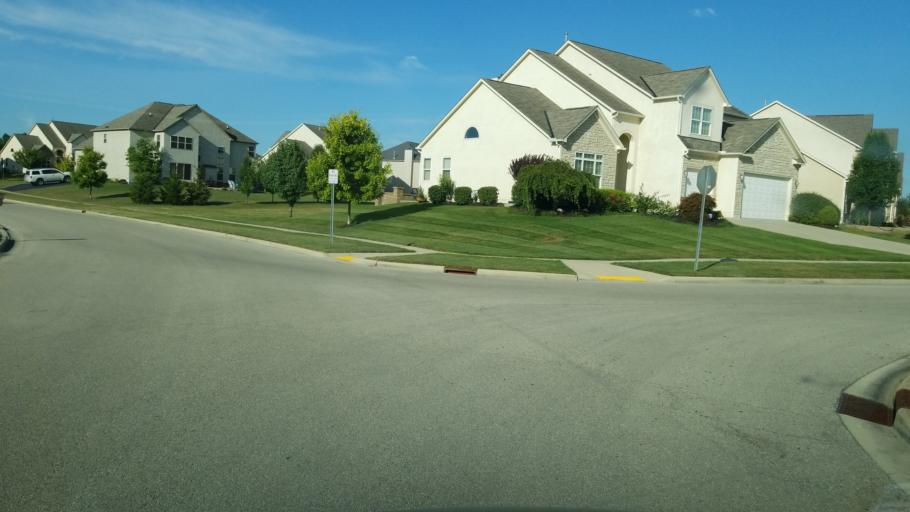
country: US
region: Ohio
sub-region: Delaware County
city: Lewis Center
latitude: 40.1863
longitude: -82.9942
